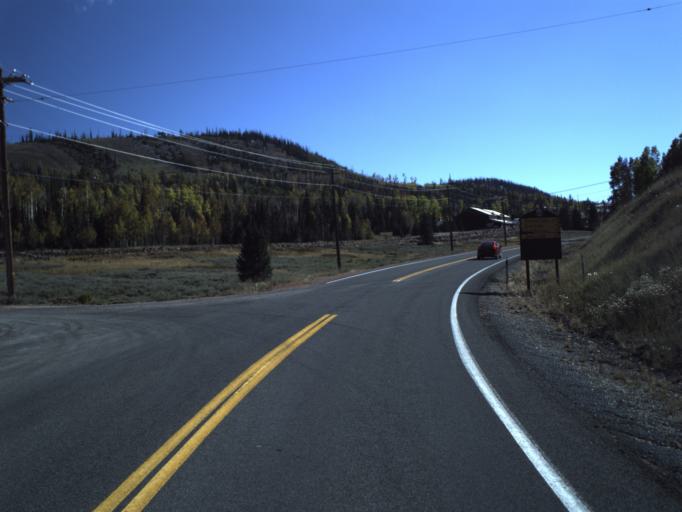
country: US
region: Utah
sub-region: Iron County
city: Parowan
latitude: 37.6984
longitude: -112.8451
